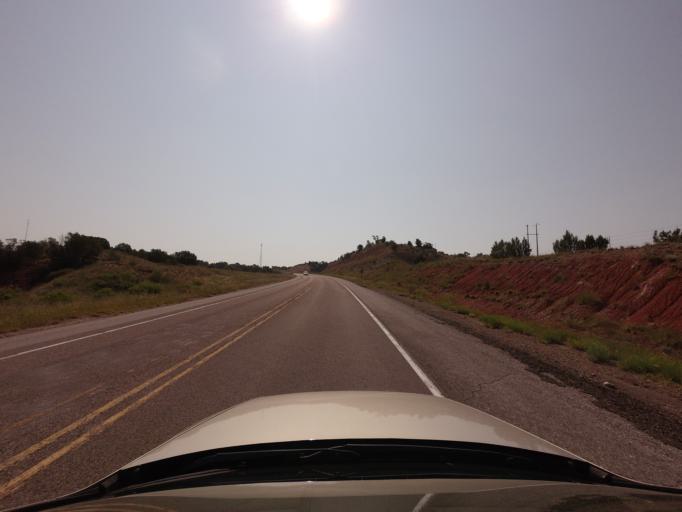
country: US
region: New Mexico
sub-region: Quay County
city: Tucumcari
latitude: 34.8242
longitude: -103.7495
